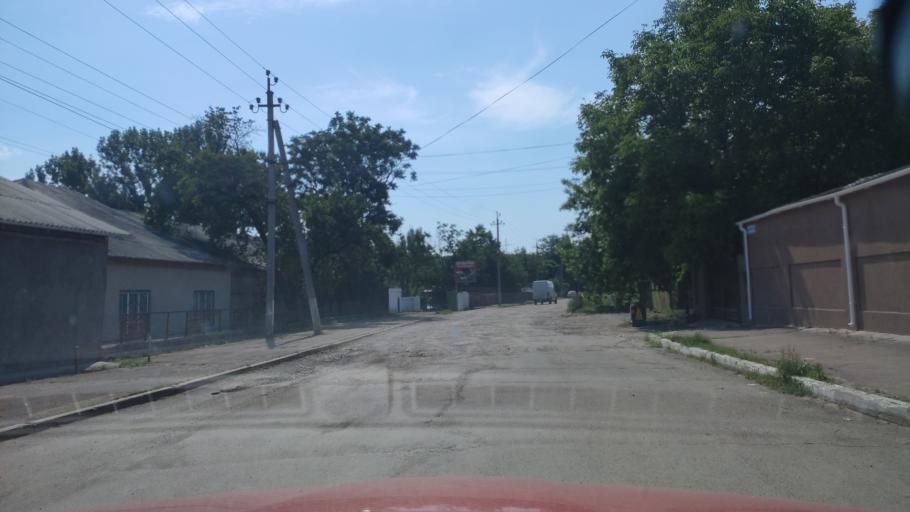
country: MD
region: Raionul Soroca
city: Soroca
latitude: 48.1719
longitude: 28.3158
